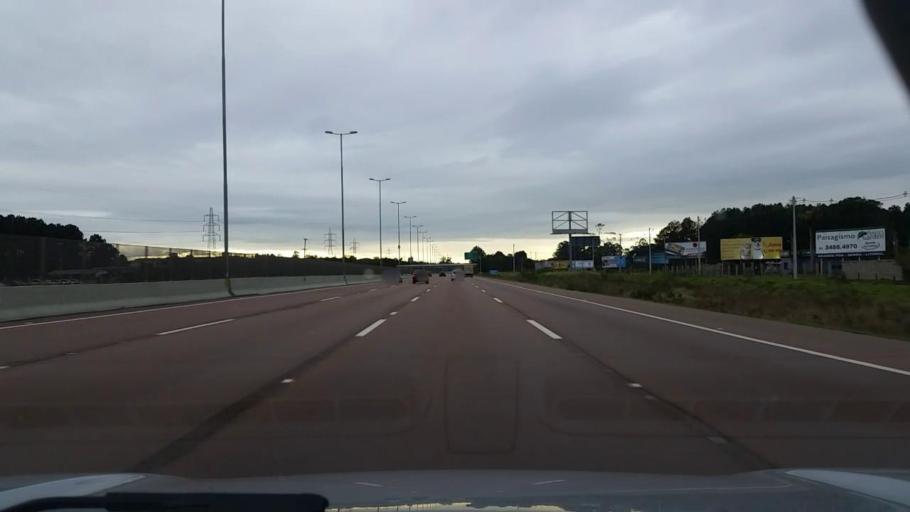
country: BR
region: Rio Grande do Sul
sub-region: Cachoeirinha
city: Cachoeirinha
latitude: -29.9542
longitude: -51.0641
